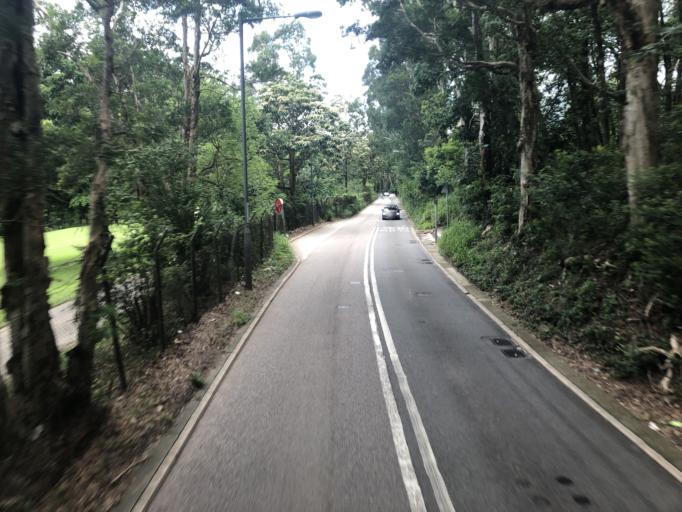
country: HK
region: Tai Po
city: Tai Po
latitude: 22.4867
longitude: 114.1163
